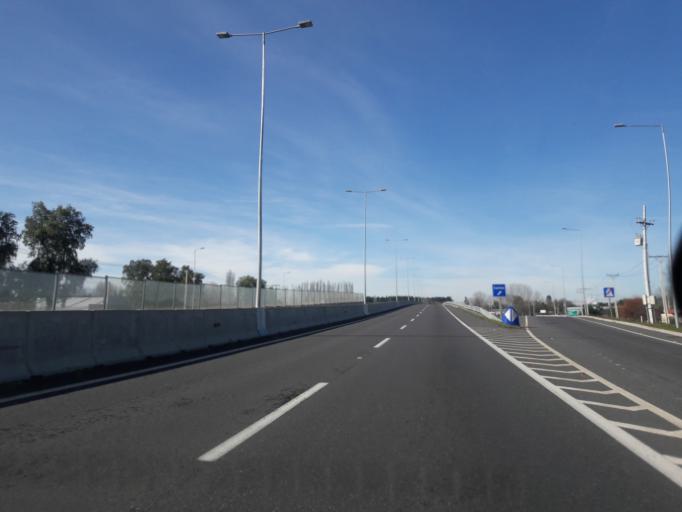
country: CL
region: Biobio
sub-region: Provincia de Biobio
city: Cabrero
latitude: -37.0300
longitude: -72.4326
